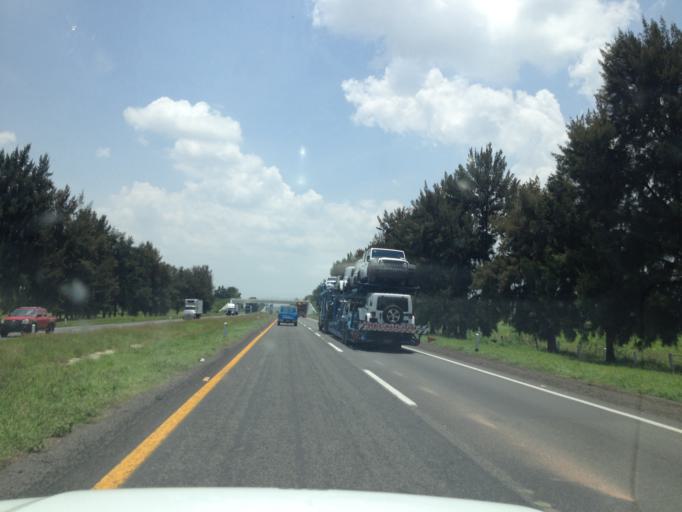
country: MX
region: Jalisco
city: La Barca
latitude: 20.3221
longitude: -102.5175
